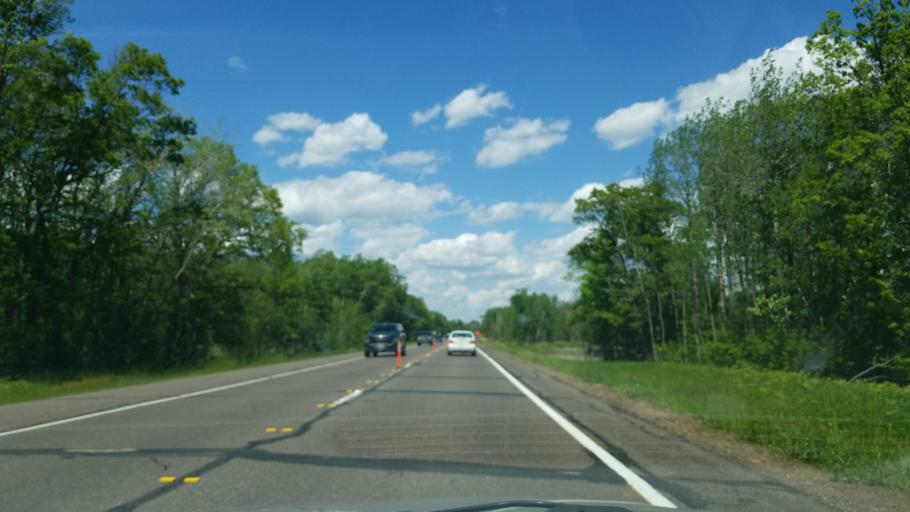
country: US
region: Minnesota
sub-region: Carlton County
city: Moose Lake
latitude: 46.3864
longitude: -92.7821
